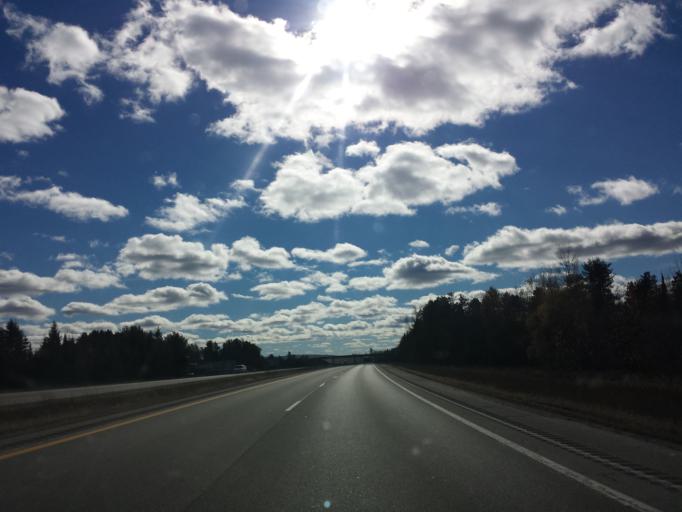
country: US
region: Michigan
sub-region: Cheboygan County
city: Indian River
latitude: 45.4156
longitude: -84.6029
